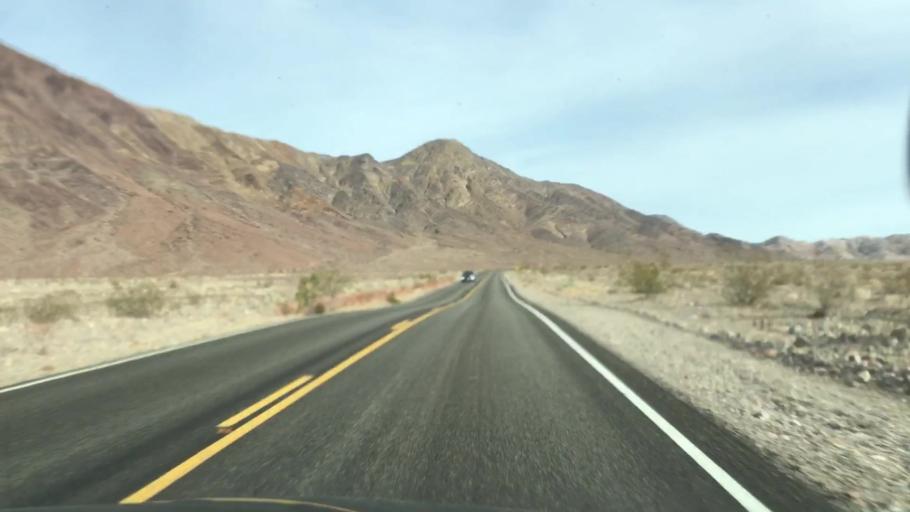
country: US
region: Nevada
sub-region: Nye County
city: Beatty
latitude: 36.6987
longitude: -116.9996
